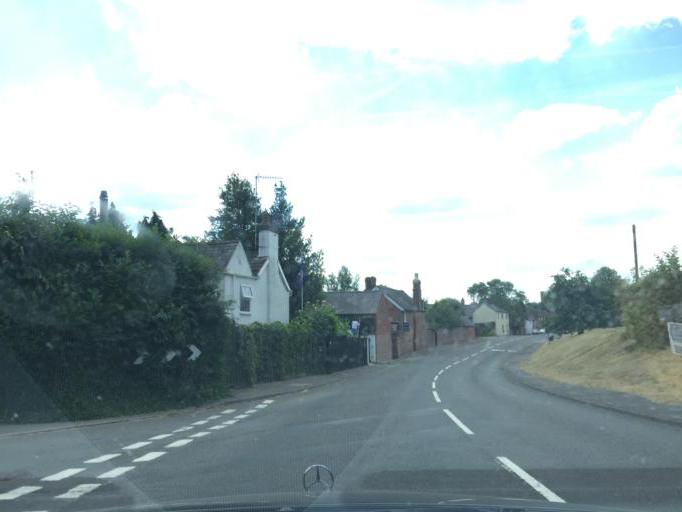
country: GB
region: England
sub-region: Warwickshire
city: Bedworth
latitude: 52.4576
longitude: -1.4033
